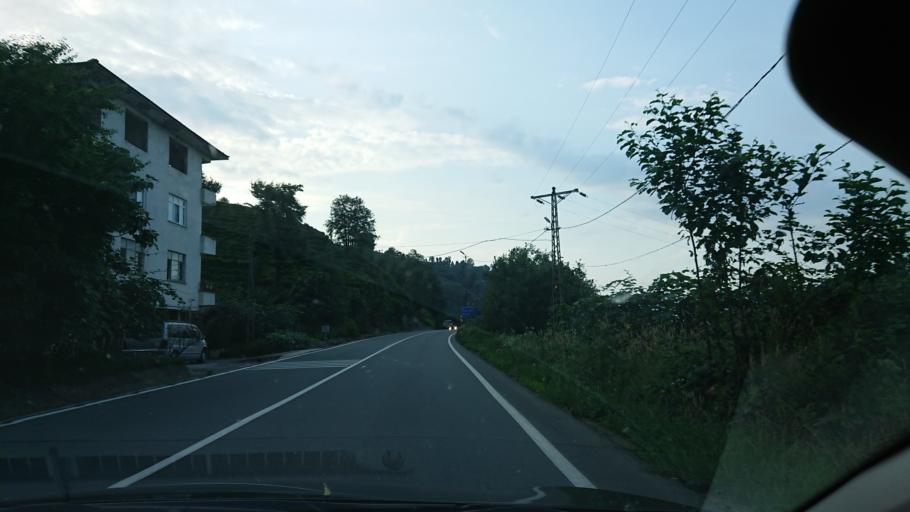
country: TR
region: Rize
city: Cayeli
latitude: 41.0670
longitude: 40.7140
